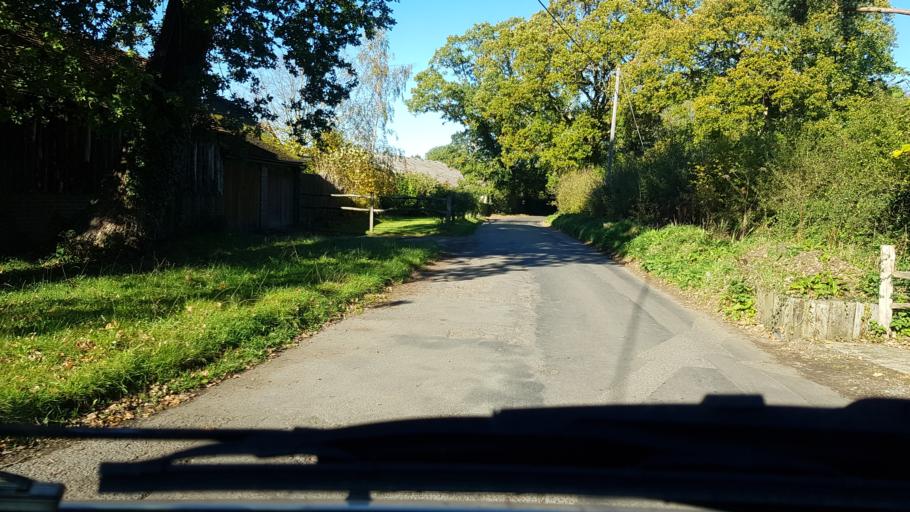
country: GB
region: England
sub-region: Surrey
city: Ockley
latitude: 51.1436
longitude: -0.3353
